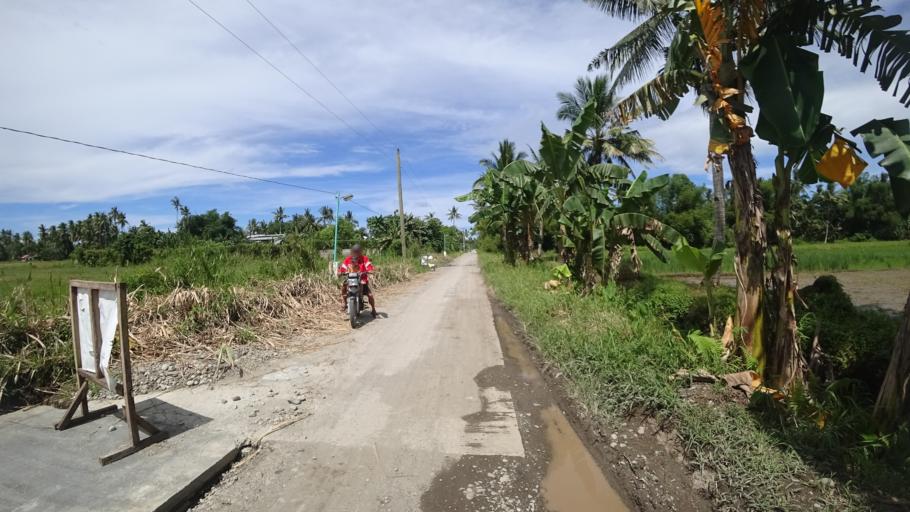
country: PH
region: Eastern Visayas
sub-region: Province of Leyte
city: Liberty
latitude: 10.8589
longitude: 124.9892
